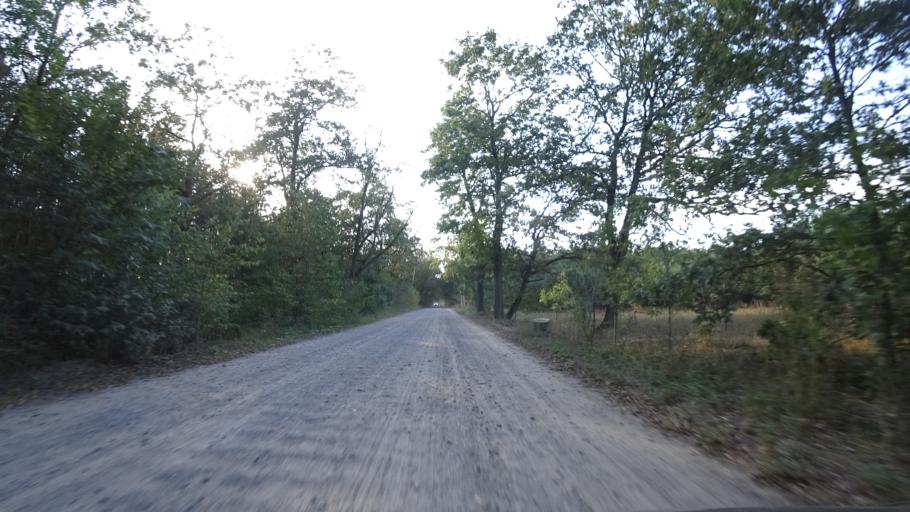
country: DE
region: Brandenburg
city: Stahnsdorf
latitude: 52.3459
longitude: 13.1705
